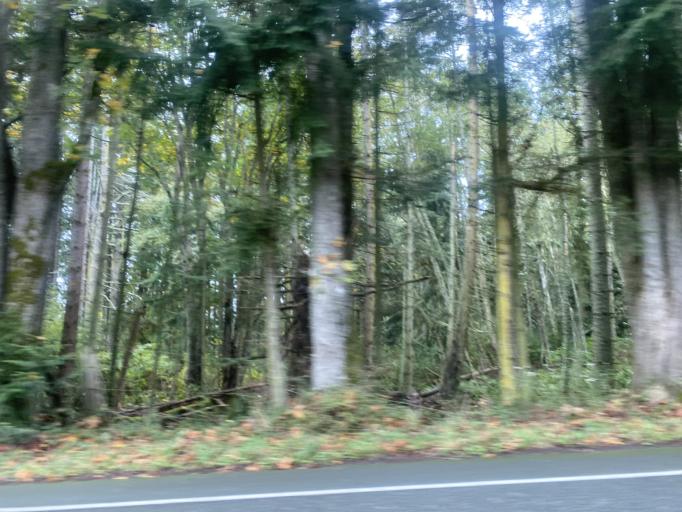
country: US
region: Washington
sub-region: Island County
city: Freeland
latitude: 48.0454
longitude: -122.5068
